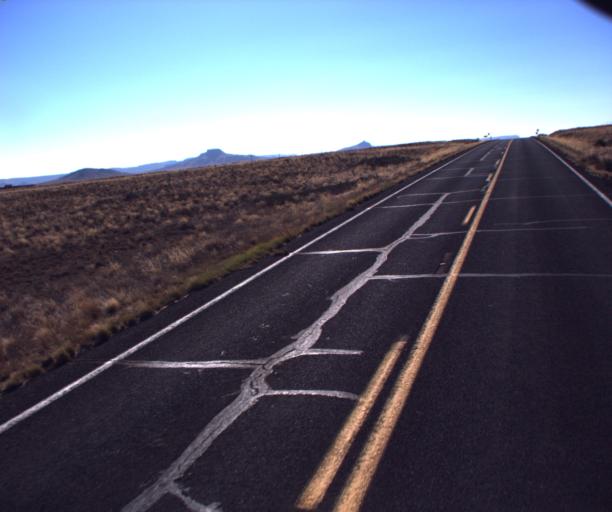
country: US
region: Arizona
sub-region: Navajo County
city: First Mesa
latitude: 35.6427
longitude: -110.4865
